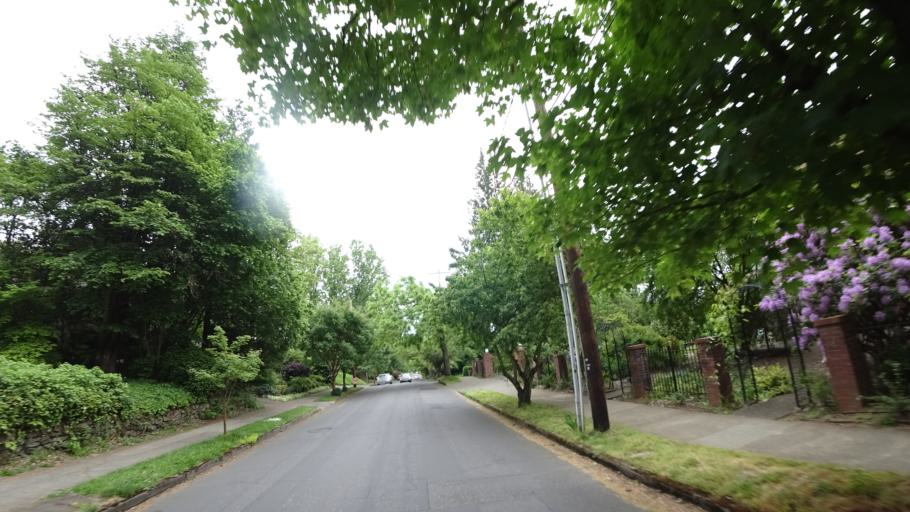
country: US
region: Oregon
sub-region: Multnomah County
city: Lents
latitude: 45.5147
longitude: -122.6067
